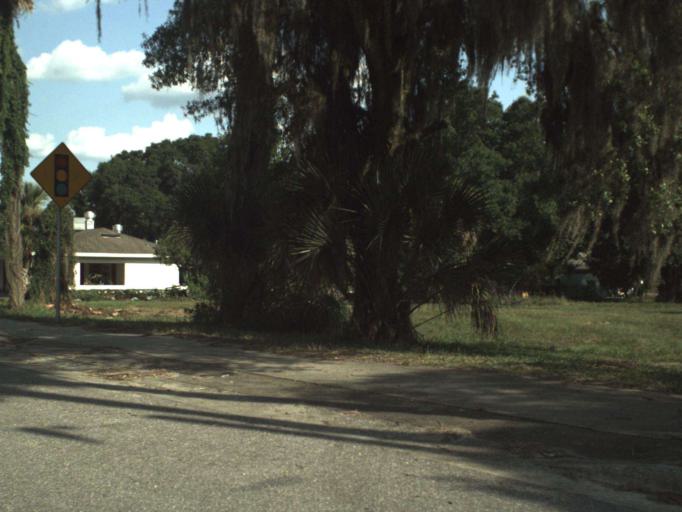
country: US
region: Florida
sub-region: Lake County
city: Groveland
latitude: 28.5588
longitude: -81.8545
